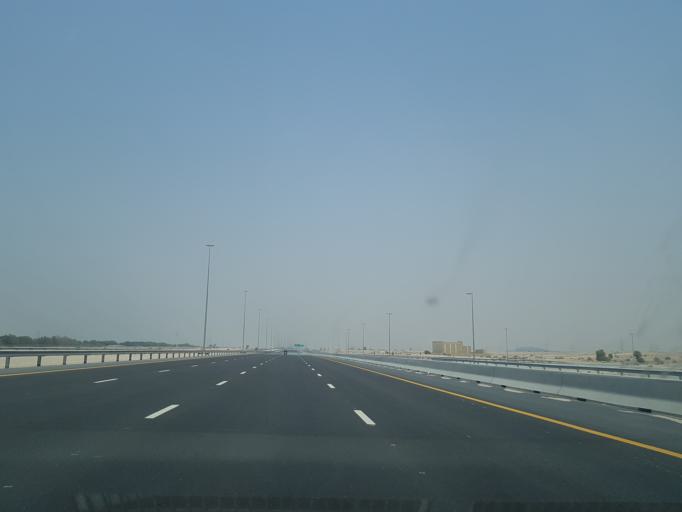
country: AE
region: Dubai
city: Dubai
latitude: 25.0472
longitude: 55.2821
